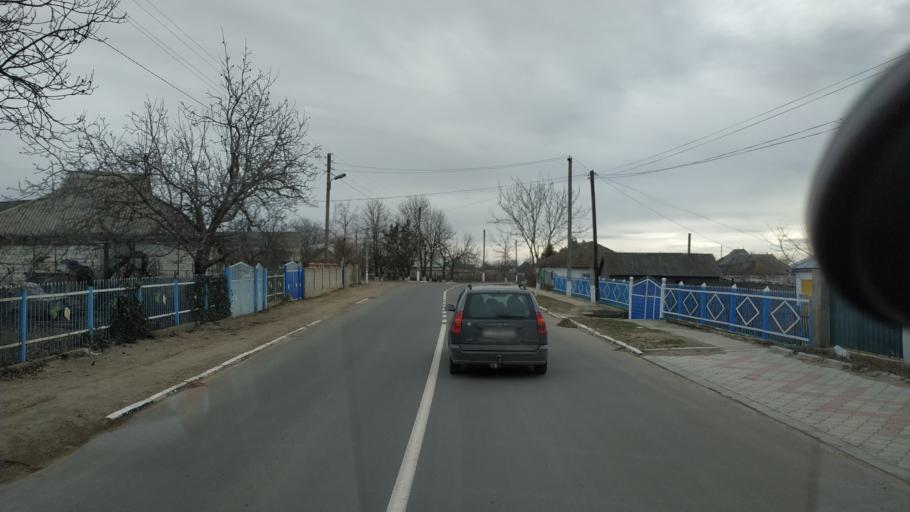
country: MD
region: Telenesti
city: Cocieri
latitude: 47.3046
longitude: 29.1123
